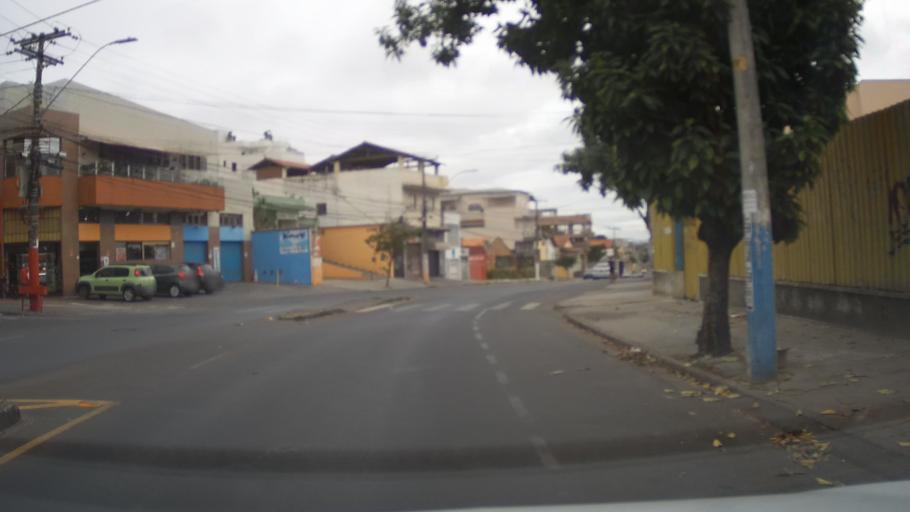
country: BR
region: Minas Gerais
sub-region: Belo Horizonte
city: Belo Horizonte
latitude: -19.8323
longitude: -43.9553
